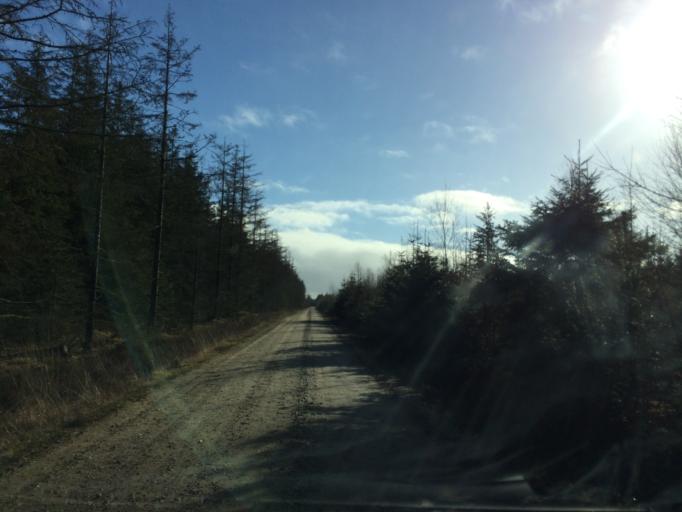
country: DK
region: Central Jutland
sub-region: Holstebro Kommune
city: Ulfborg
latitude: 56.2718
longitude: 8.3835
